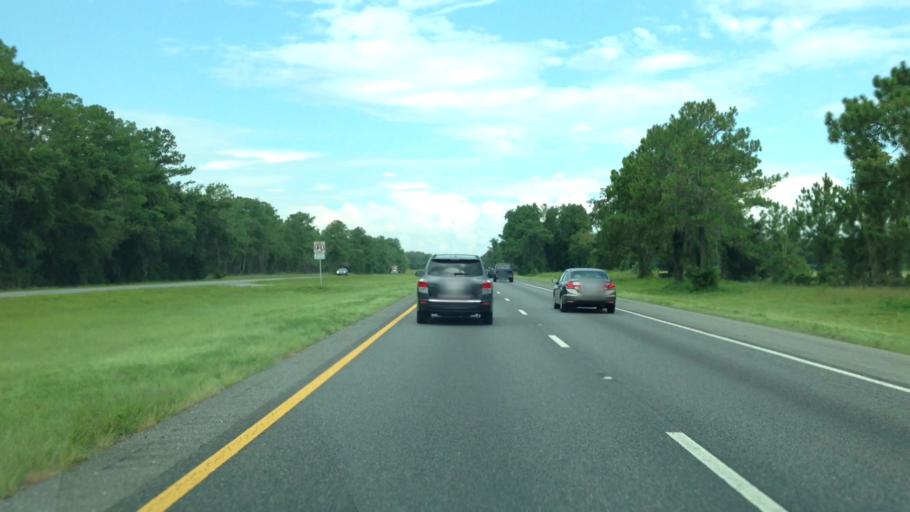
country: US
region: Florida
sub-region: Suwannee County
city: Live Oak
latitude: 30.3057
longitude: -82.9203
